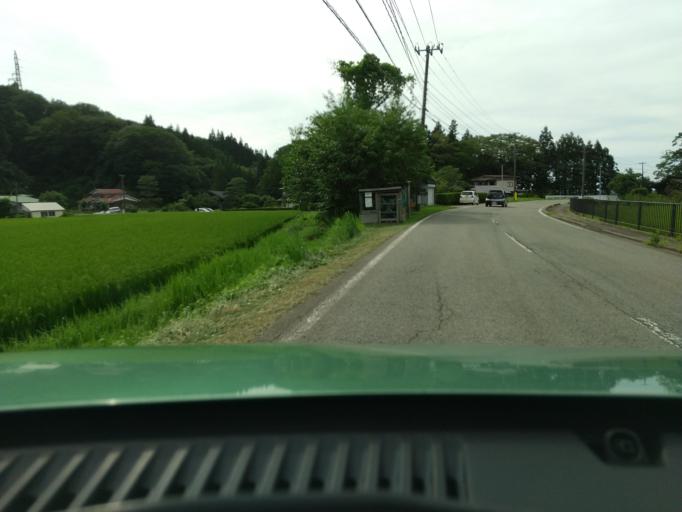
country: JP
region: Akita
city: Akita Shi
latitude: 39.7894
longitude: 140.1143
